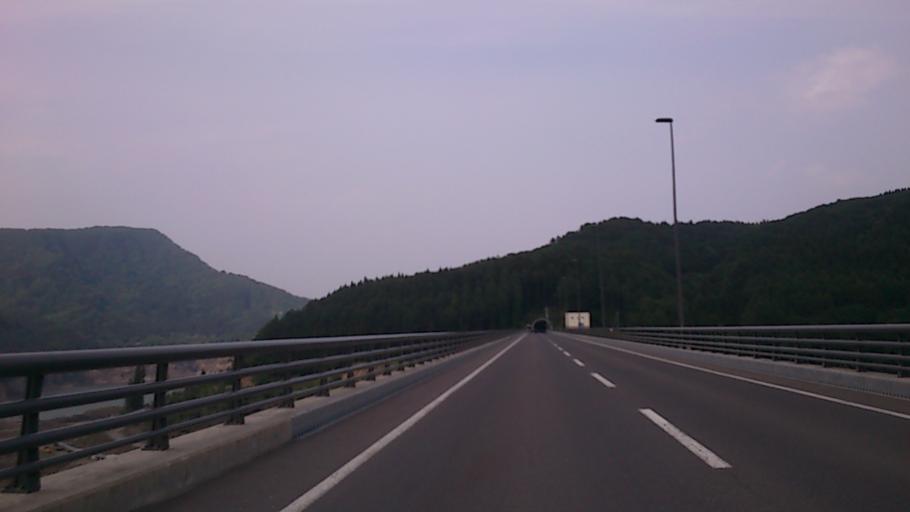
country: JP
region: Aomori
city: Hirosaki
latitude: 40.5296
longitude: 140.2432
